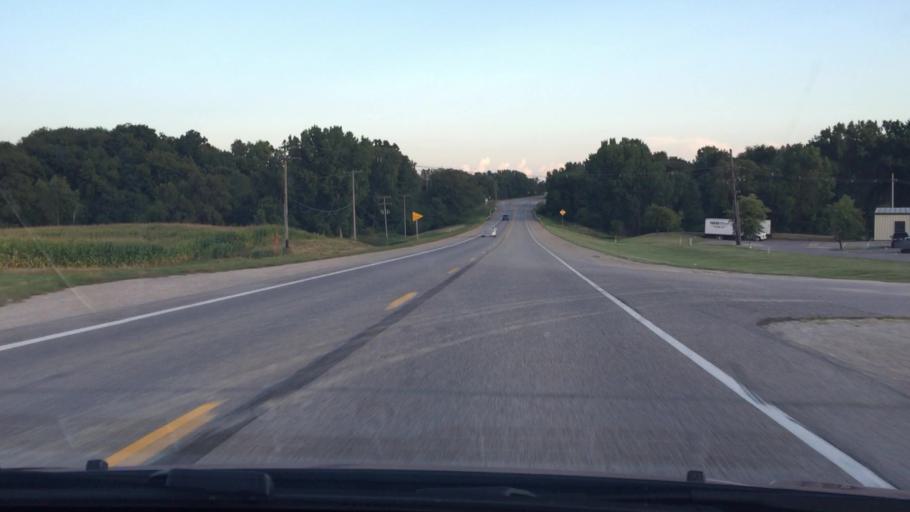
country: US
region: Iowa
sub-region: Muscatine County
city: Muscatine
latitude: 41.4626
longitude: -91.0328
